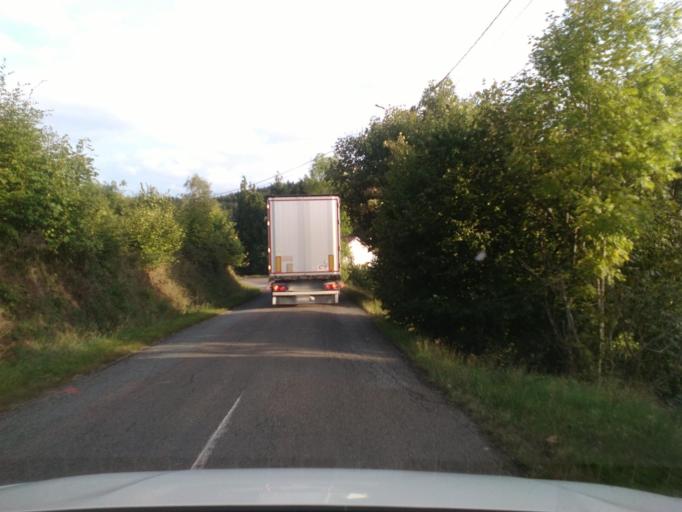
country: FR
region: Lorraine
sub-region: Departement des Vosges
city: Ban-de-Laveline
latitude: 48.3223
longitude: 7.0541
